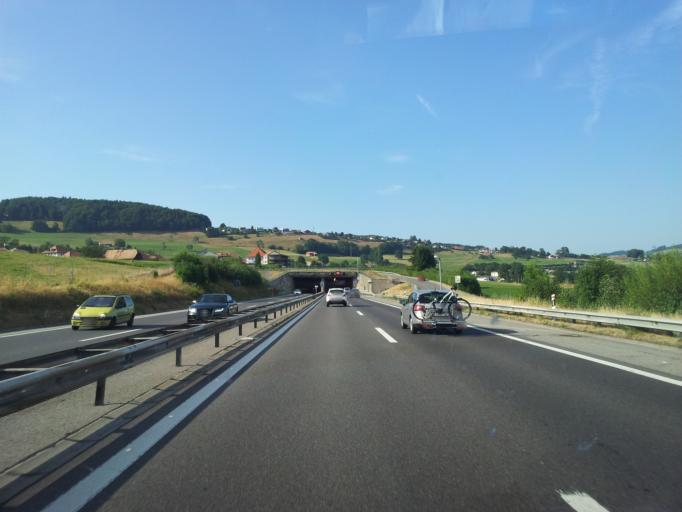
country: CH
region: Fribourg
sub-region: Gruyere District
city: Marsens
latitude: 46.6730
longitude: 7.0764
